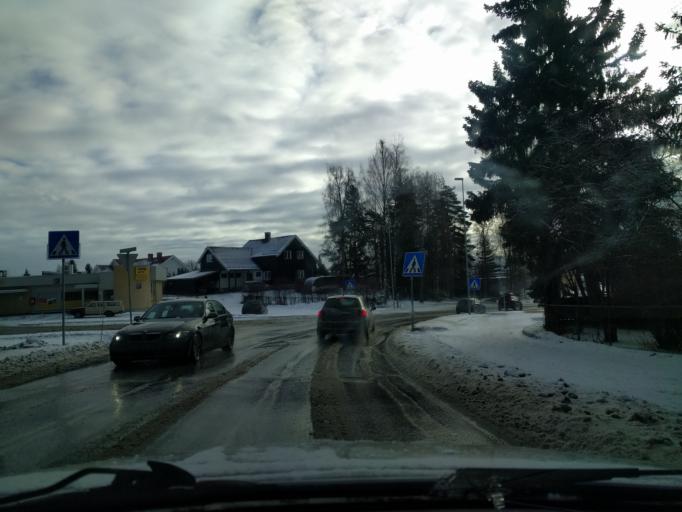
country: NO
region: Hedmark
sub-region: Hamar
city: Hamar
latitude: 60.7990
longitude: 11.0880
